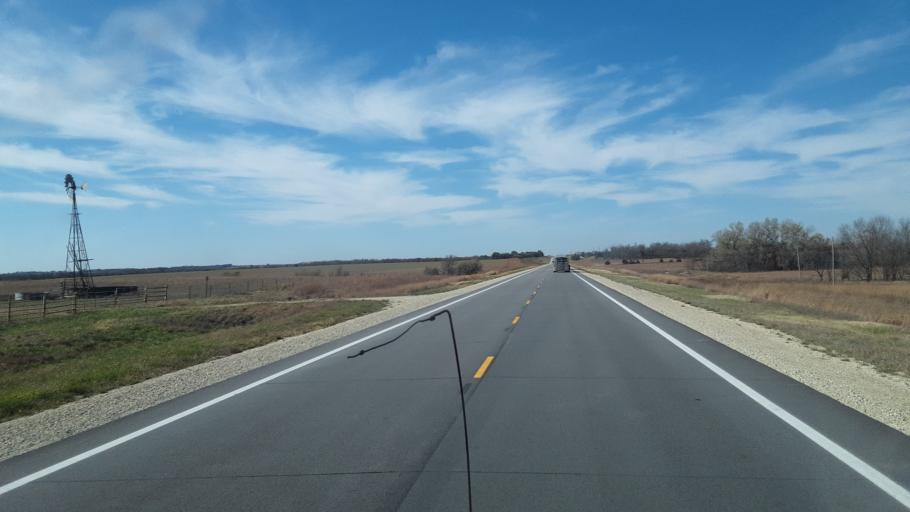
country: US
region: Kansas
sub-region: Marion County
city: Marion
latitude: 38.3624
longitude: -96.8466
